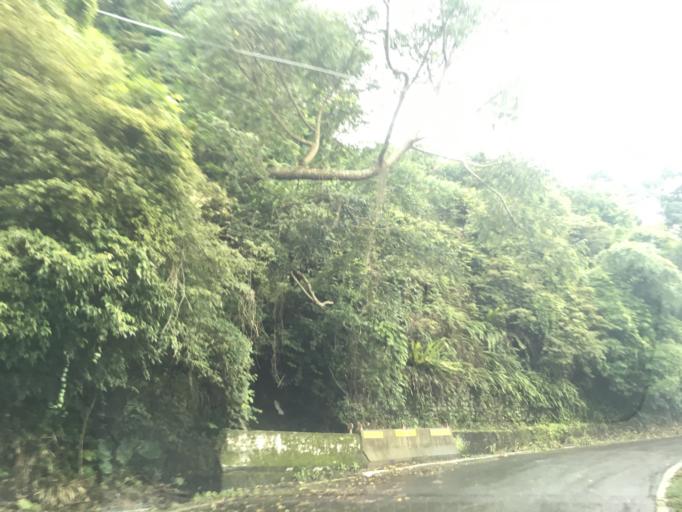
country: TW
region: Taiwan
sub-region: Yunlin
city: Douliu
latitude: 23.5606
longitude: 120.6621
